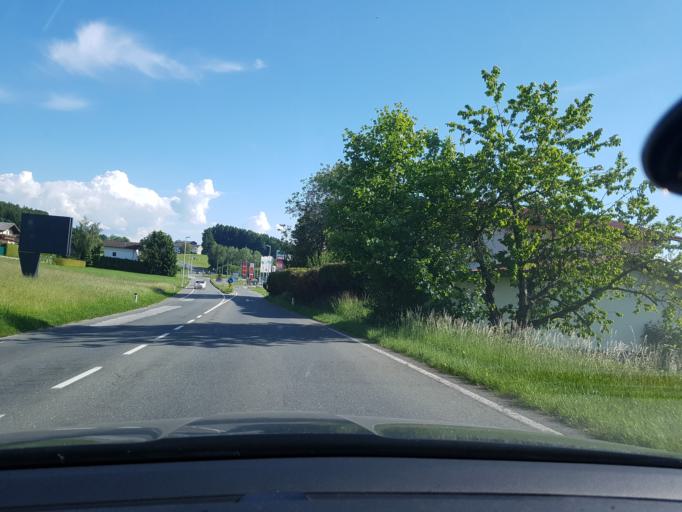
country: AT
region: Salzburg
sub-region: Politischer Bezirk Salzburg-Umgebung
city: Obertrum am See
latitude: 47.9346
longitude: 13.0807
